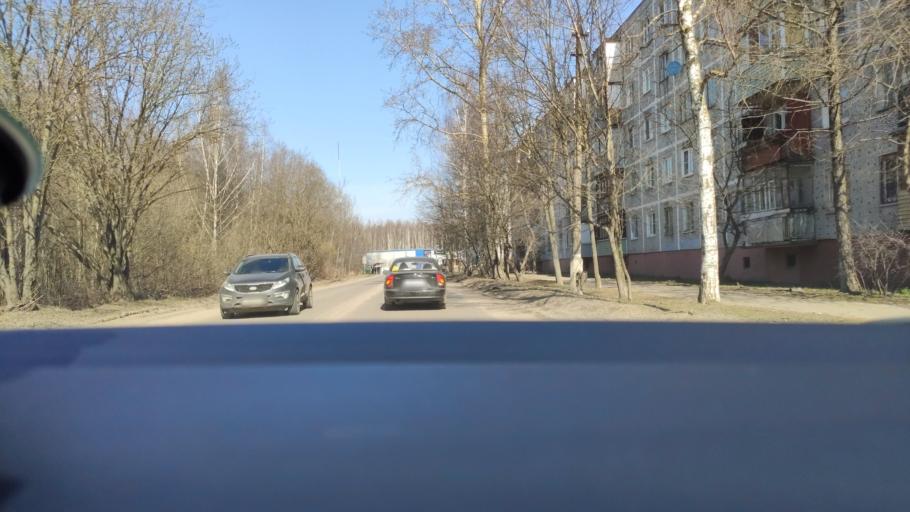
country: RU
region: Moskovskaya
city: Elektrostal'
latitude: 55.7681
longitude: 38.4172
